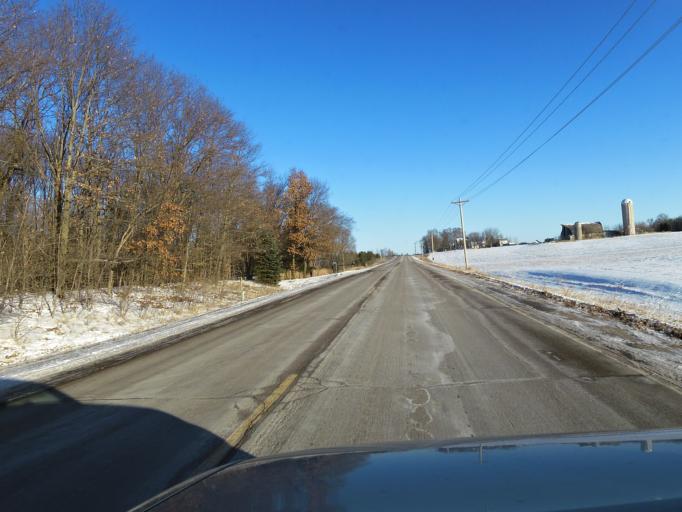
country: US
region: Minnesota
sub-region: Scott County
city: Jordan
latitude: 44.6489
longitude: -93.5625
